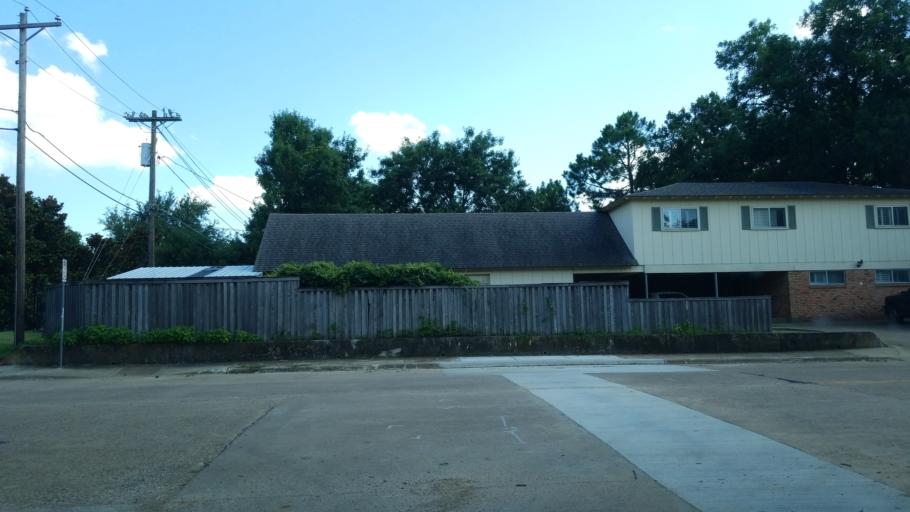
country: US
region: Texas
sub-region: Dallas County
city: University Park
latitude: 32.8879
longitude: -96.8429
